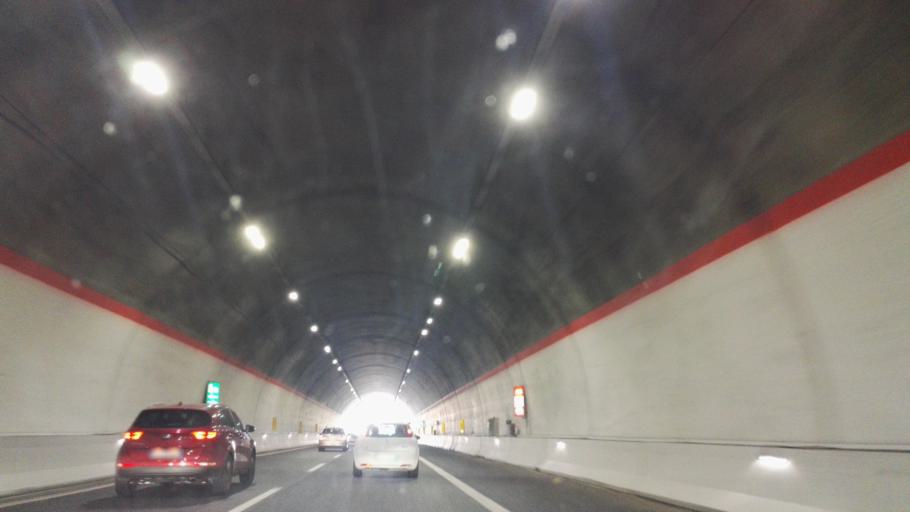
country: IT
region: Calabria
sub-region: Provincia di Cosenza
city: Rosario
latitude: 39.3035
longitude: 16.2365
